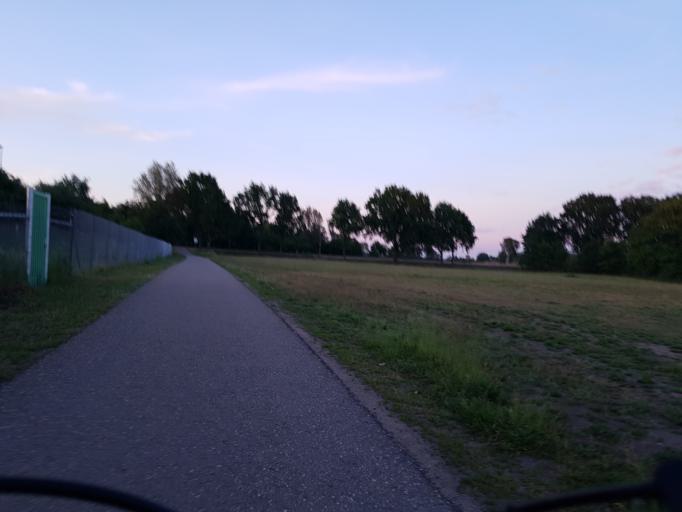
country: DE
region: Brandenburg
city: Falkenberg
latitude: 51.6082
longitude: 13.3049
